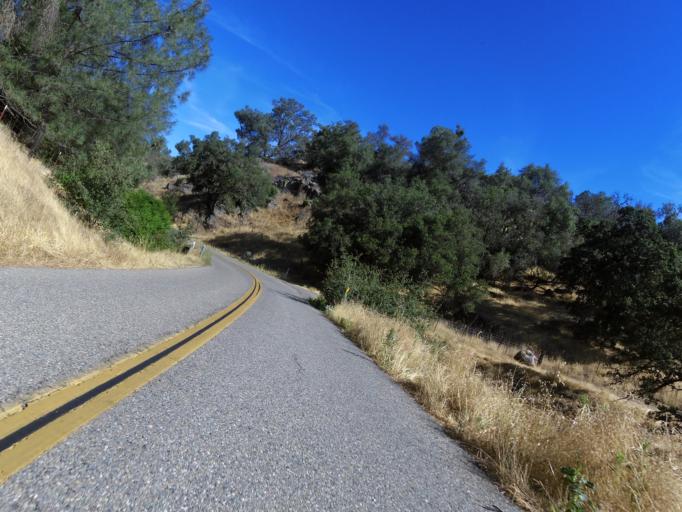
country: US
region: California
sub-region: Mariposa County
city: Mariposa
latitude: 37.2854
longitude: -119.9751
